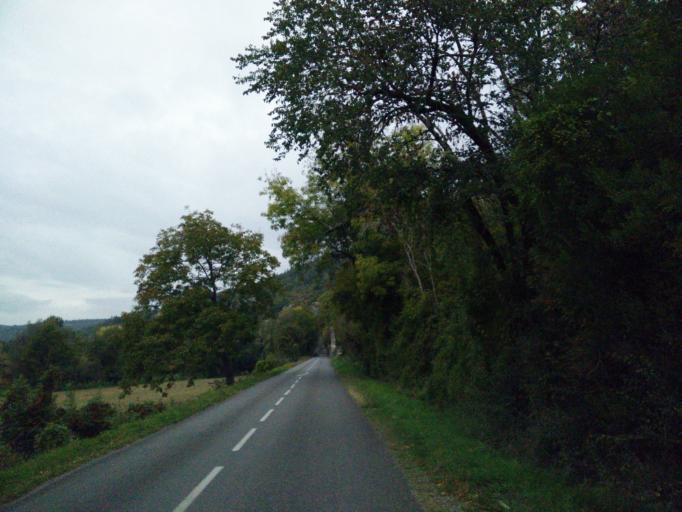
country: FR
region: Midi-Pyrenees
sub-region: Departement du Lot
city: Lalbenque
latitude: 44.4801
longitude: 1.6488
